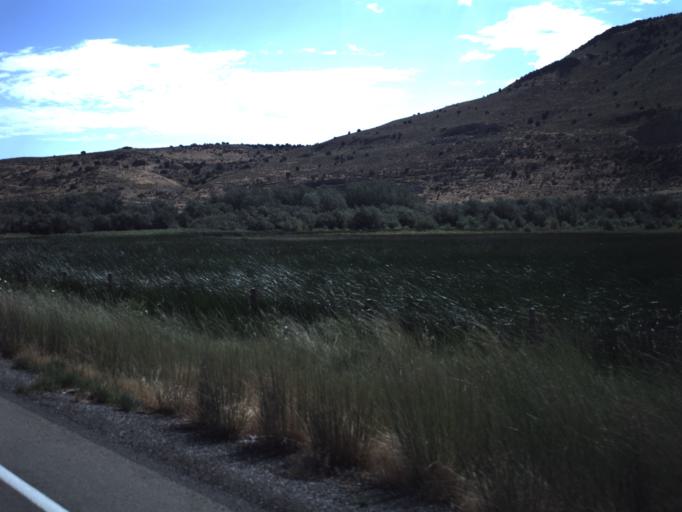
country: US
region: Utah
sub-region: Utah County
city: Genola
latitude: 39.9666
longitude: -111.8580
